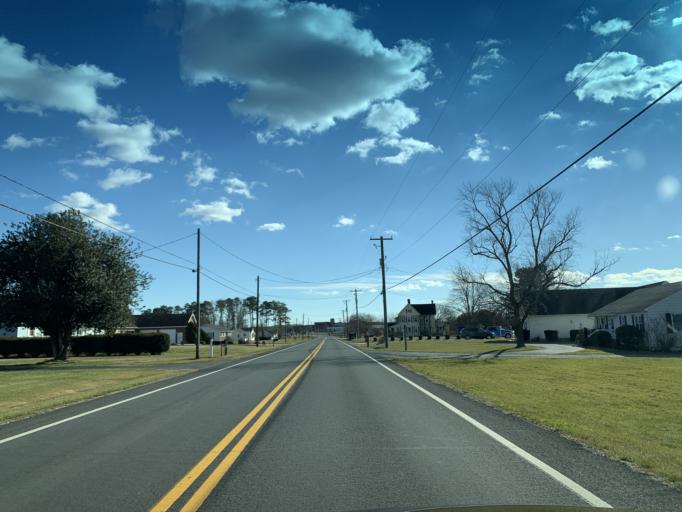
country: US
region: Maryland
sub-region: Worcester County
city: Berlin
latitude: 38.3474
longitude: -75.1921
